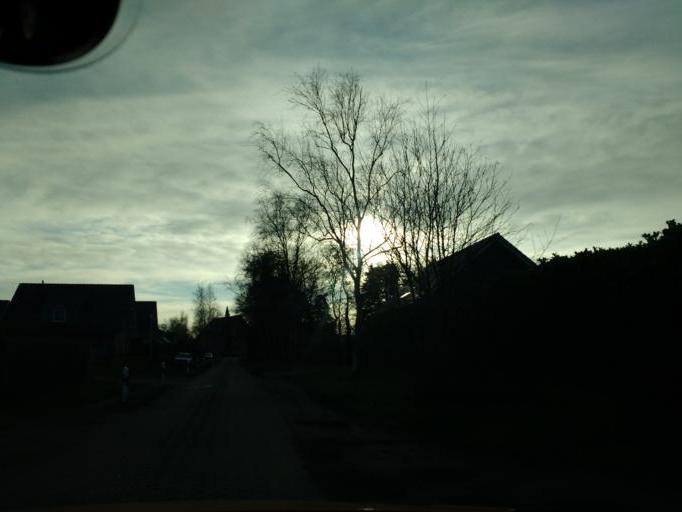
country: DE
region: Lower Saxony
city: Hude
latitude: 53.1130
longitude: 8.4716
